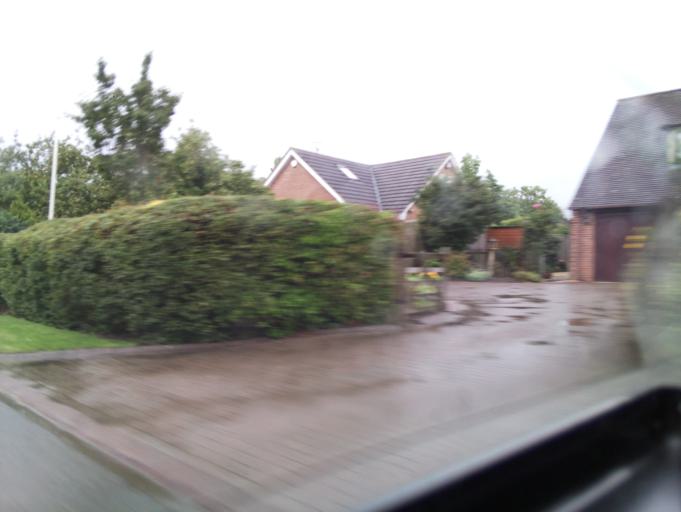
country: GB
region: England
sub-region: Gloucestershire
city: Tewkesbury
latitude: 51.9642
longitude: -2.1414
